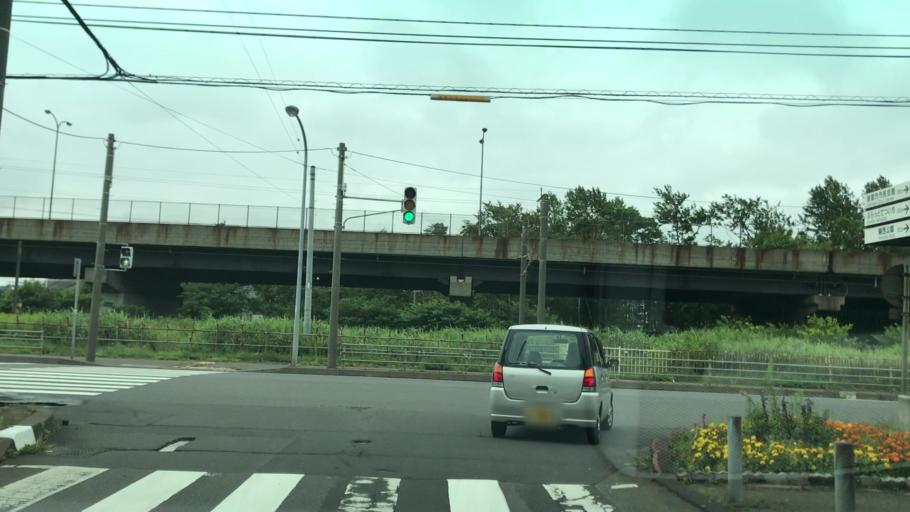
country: JP
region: Hokkaido
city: Muroran
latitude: 42.3352
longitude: 141.0104
